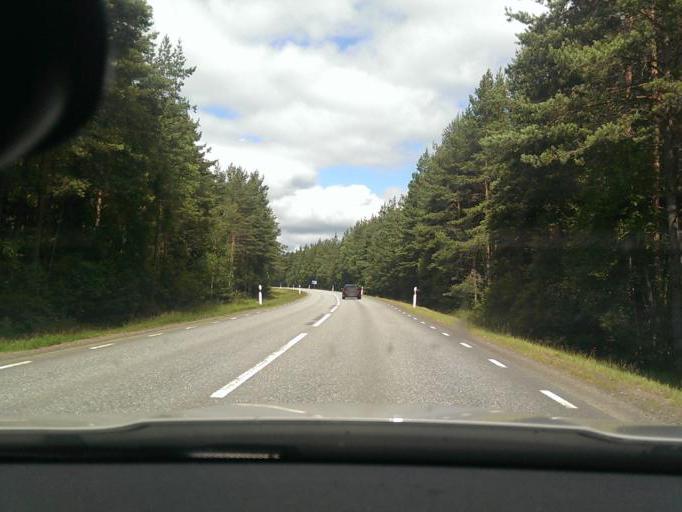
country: SE
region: Joenkoeping
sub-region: Gnosjo Kommun
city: Hillerstorp
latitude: 57.2849
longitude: 13.9638
